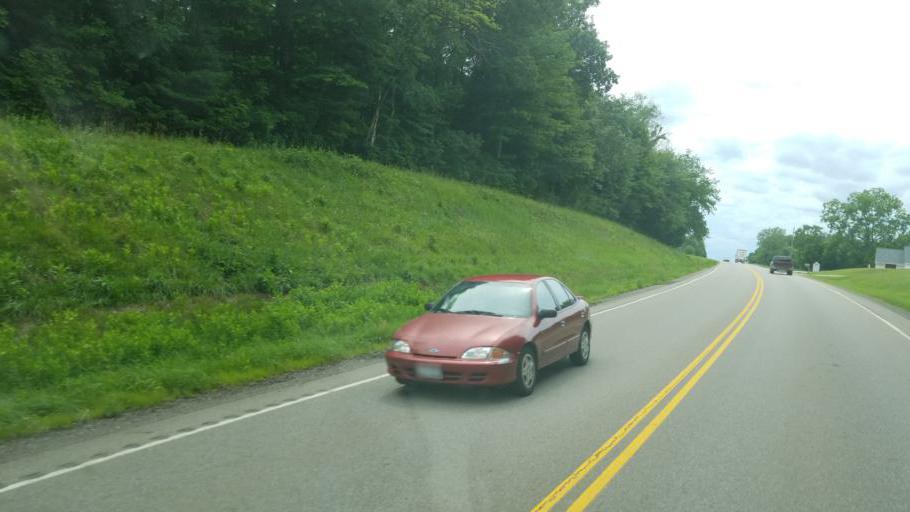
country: US
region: Ohio
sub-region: Licking County
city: Utica
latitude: 40.2320
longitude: -82.4713
